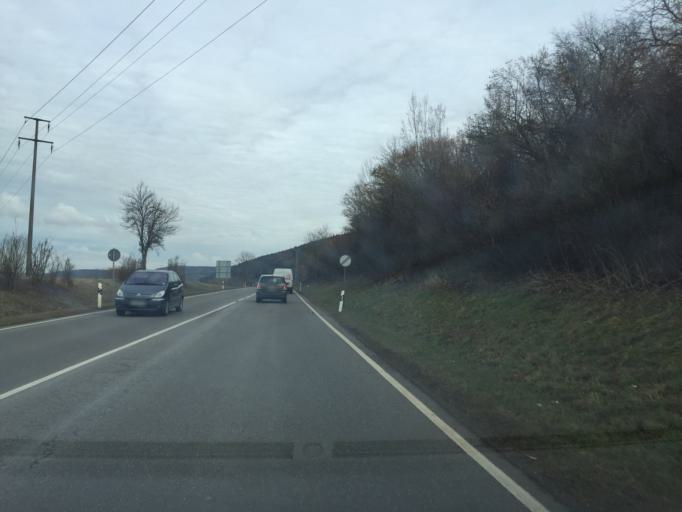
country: DE
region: Baden-Wuerttemberg
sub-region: Freiburg Region
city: Geisingen
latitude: 47.9167
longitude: 8.6362
